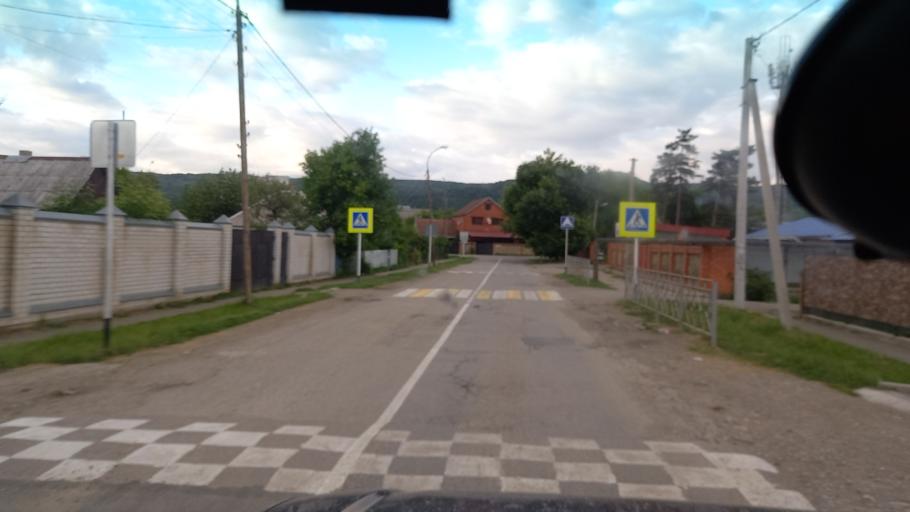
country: RU
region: Krasnodarskiy
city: Apsheronsk
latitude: 44.4563
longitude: 39.7490
